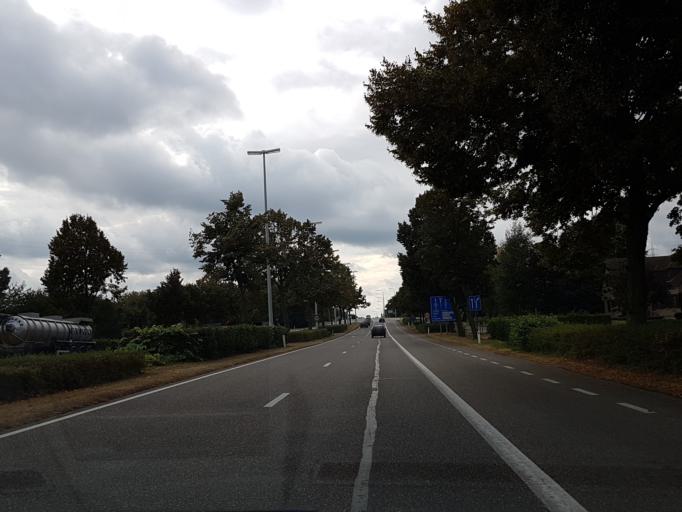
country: BE
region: Flanders
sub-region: Provincie Limburg
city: Sint-Truiden
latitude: 50.8078
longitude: 5.1871
